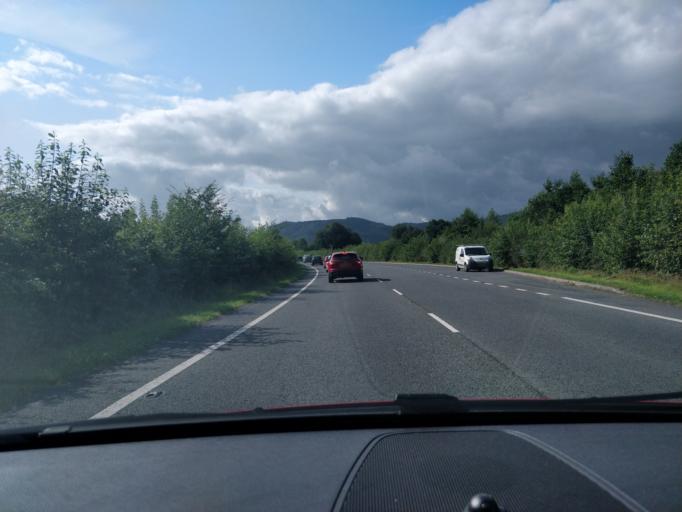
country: GB
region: Wales
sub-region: Conwy
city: Llanrwst
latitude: 53.1594
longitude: -3.8113
